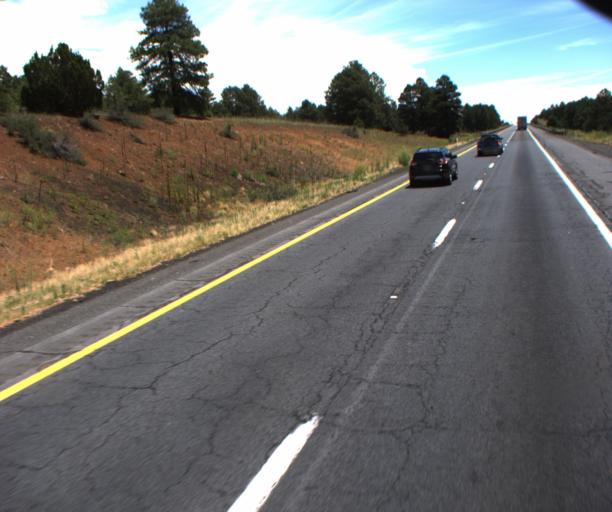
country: US
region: Arizona
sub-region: Coconino County
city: Parks
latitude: 35.2563
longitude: -112.0160
